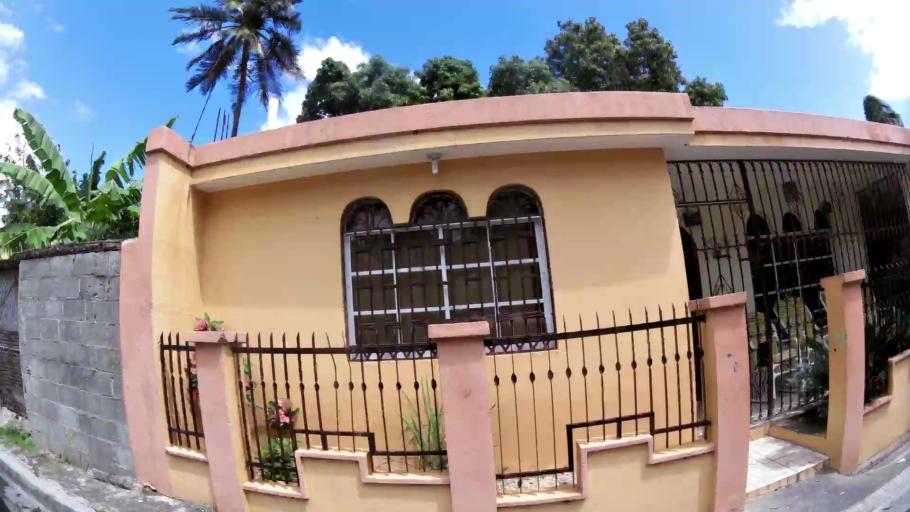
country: DO
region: San Cristobal
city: San Cristobal
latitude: 18.4165
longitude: -70.0978
